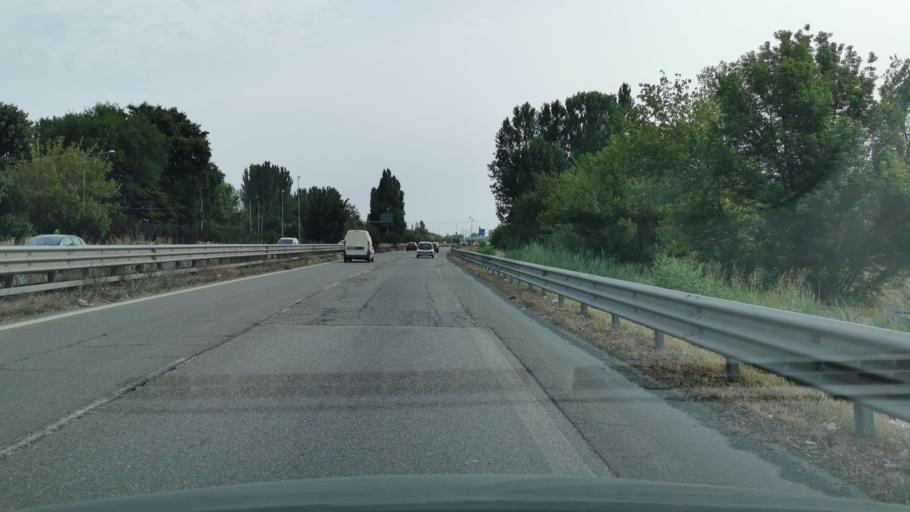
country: IT
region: Emilia-Romagna
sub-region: Provincia di Modena
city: Modena
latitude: 44.6280
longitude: 10.9523
